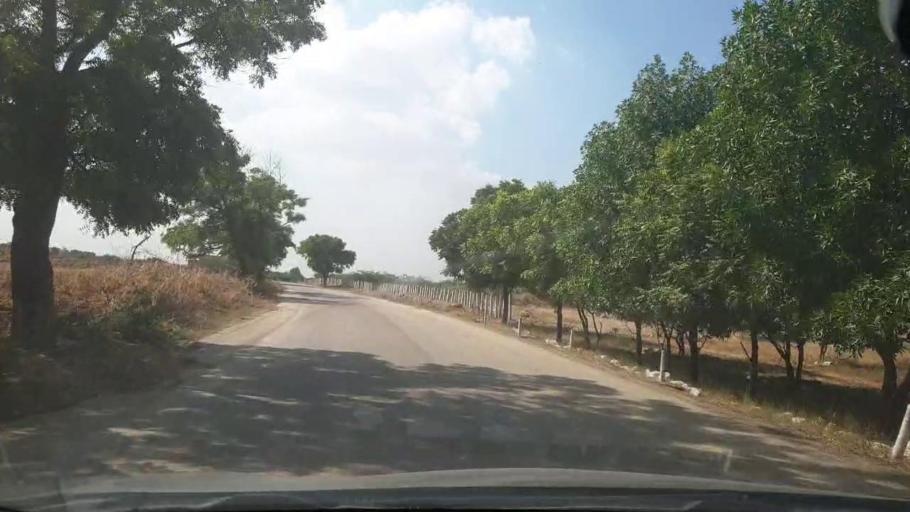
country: PK
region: Sindh
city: Malir Cantonment
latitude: 25.0257
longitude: 67.3595
